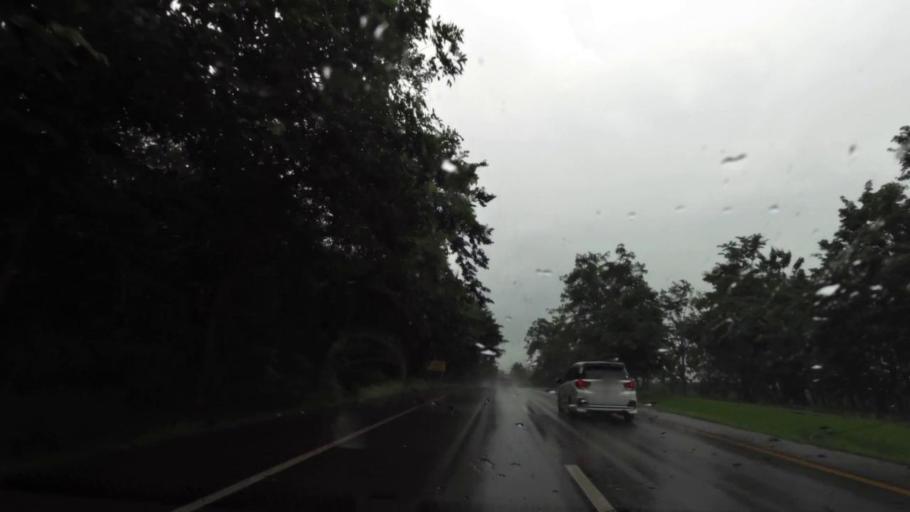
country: TH
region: Chon Buri
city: Nong Yai
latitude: 13.0490
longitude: 101.4297
